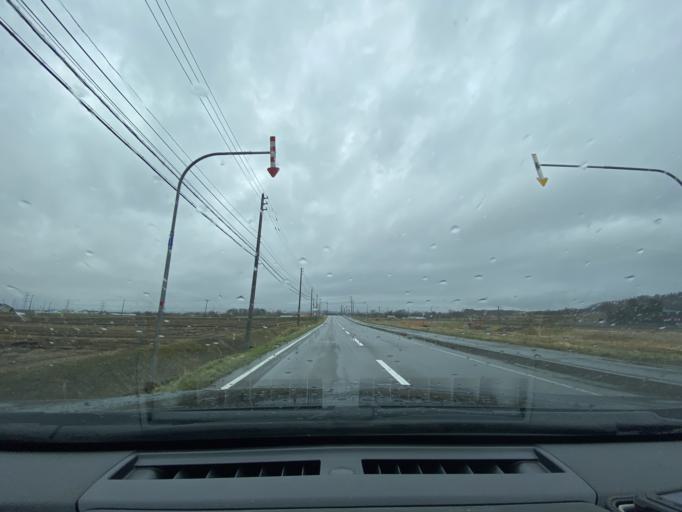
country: JP
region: Hokkaido
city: Fukagawa
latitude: 43.8134
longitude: 141.9616
